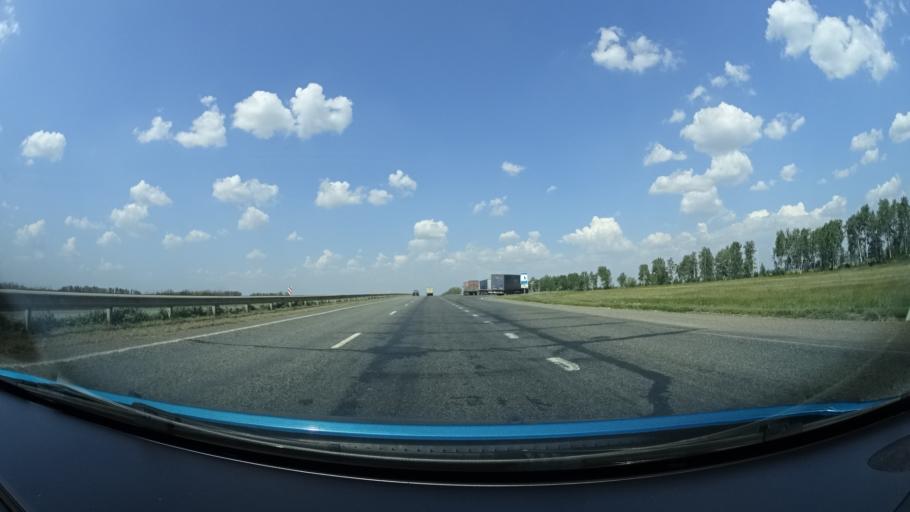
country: RU
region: Bashkortostan
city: Dmitriyevka
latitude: 54.6895
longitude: 55.3005
